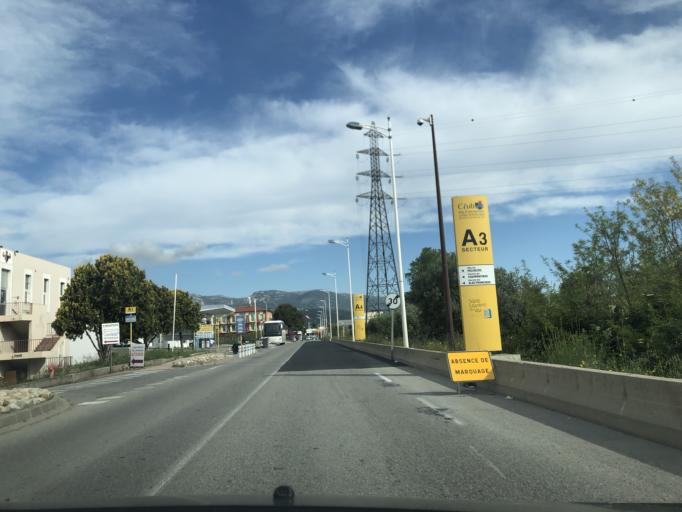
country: FR
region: Provence-Alpes-Cote d'Azur
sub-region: Departement des Alpes-Maritimes
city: Saint-Laurent-du-Var
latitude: 43.6854
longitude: 7.1878
